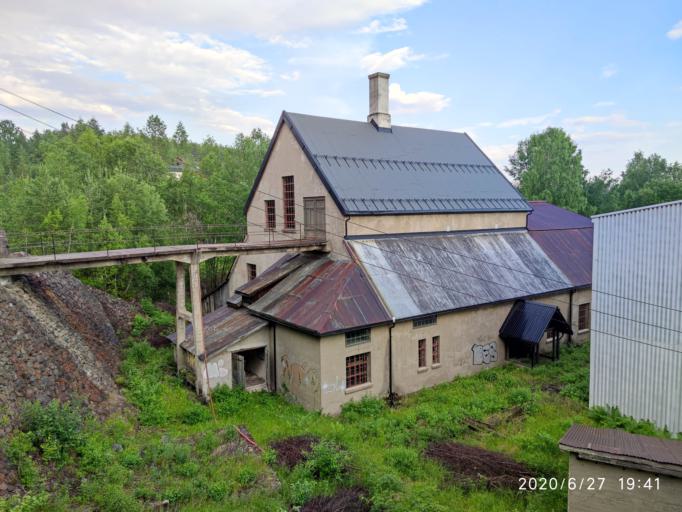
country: NO
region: Buskerud
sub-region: Kongsberg
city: Kongsberg
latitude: 59.6296
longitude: 9.6003
